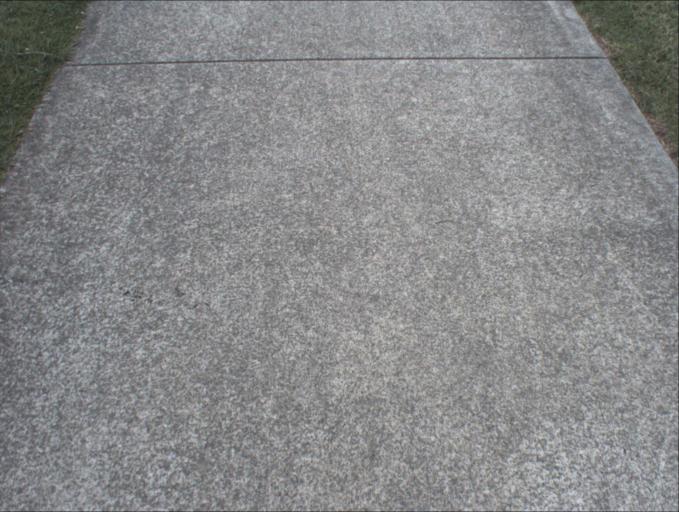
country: AU
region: Queensland
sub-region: Logan
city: Slacks Creek
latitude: -27.6702
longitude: 153.1579
